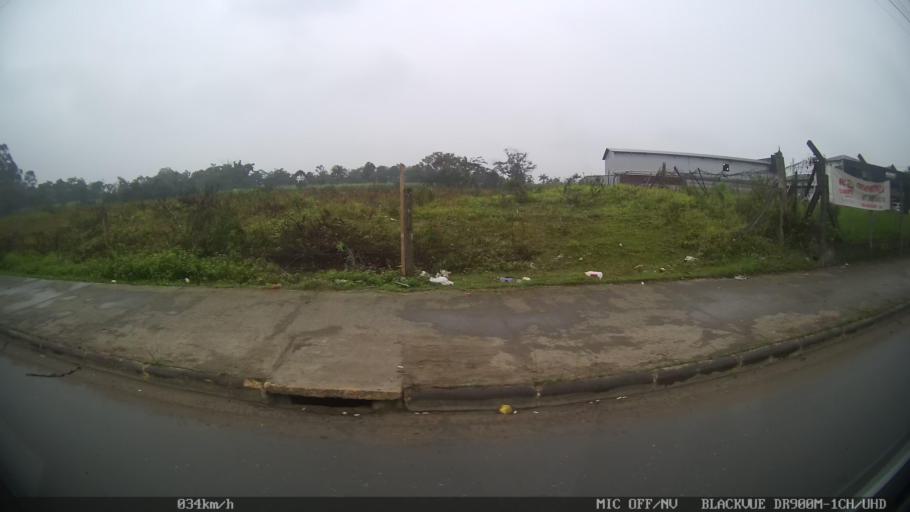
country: BR
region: Santa Catarina
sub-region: Joinville
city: Joinville
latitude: -26.2268
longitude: -48.8190
